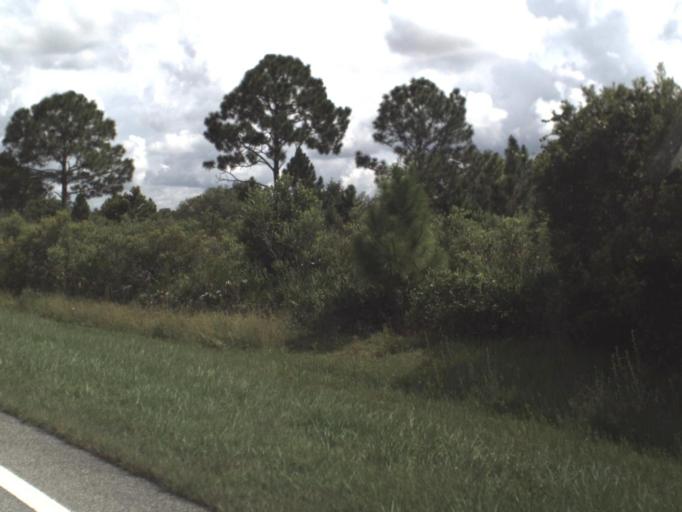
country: US
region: Florida
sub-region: Sarasota County
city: Lake Sarasota
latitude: 27.2224
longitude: -82.2949
